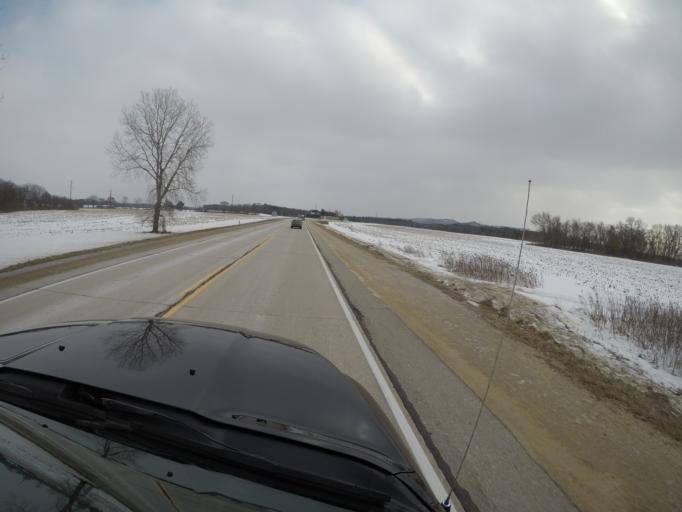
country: US
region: Wisconsin
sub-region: Trempealeau County
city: Galesville
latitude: 44.0697
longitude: -91.2973
